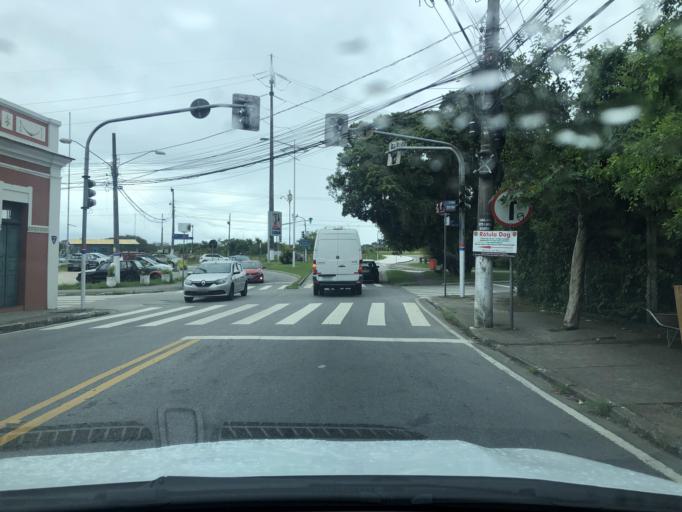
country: BR
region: Santa Catarina
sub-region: Florianopolis
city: Saco dos Limoes
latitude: -27.6134
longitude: -48.5267
